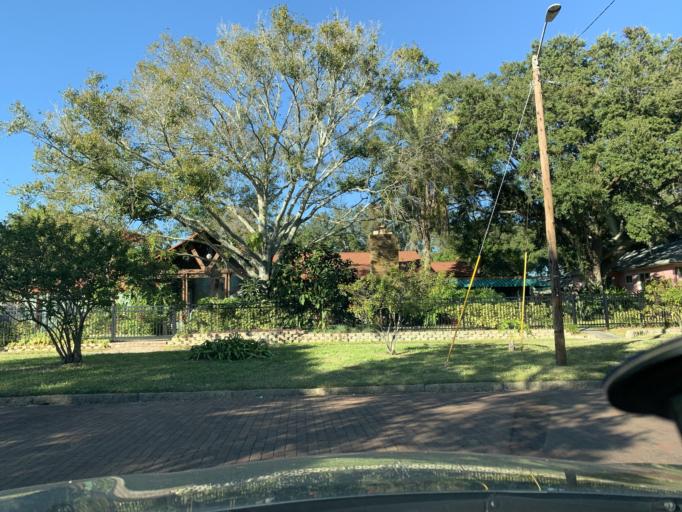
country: US
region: Florida
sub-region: Pinellas County
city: Gulfport
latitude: 27.7434
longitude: -82.7011
